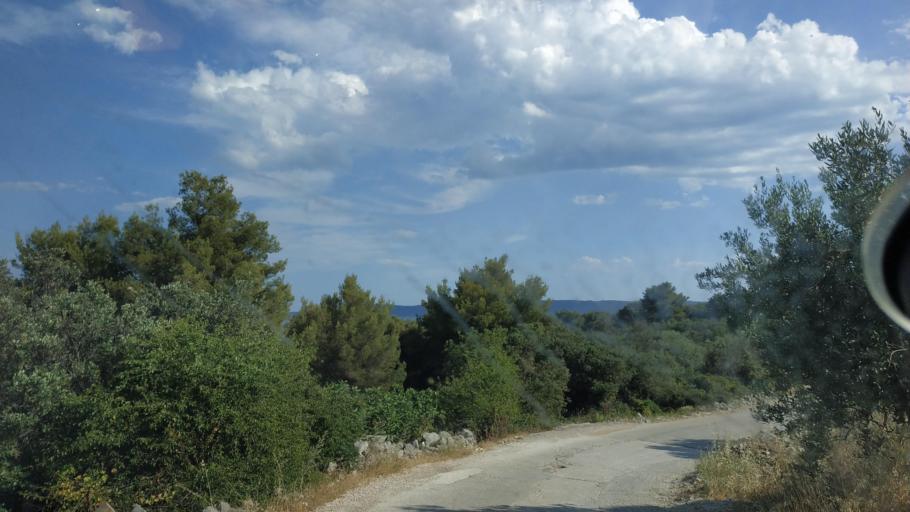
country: HR
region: Splitsko-Dalmatinska
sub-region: Grad Trogir
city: Trogir
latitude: 43.4854
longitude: 16.2453
